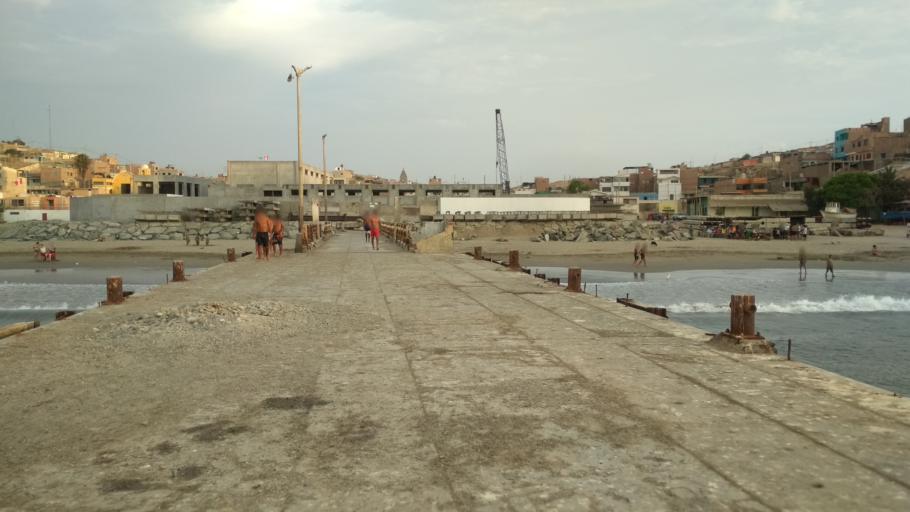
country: PE
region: Lima
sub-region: Barranca
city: Puerto Supe
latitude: -10.8002
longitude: -77.7470
